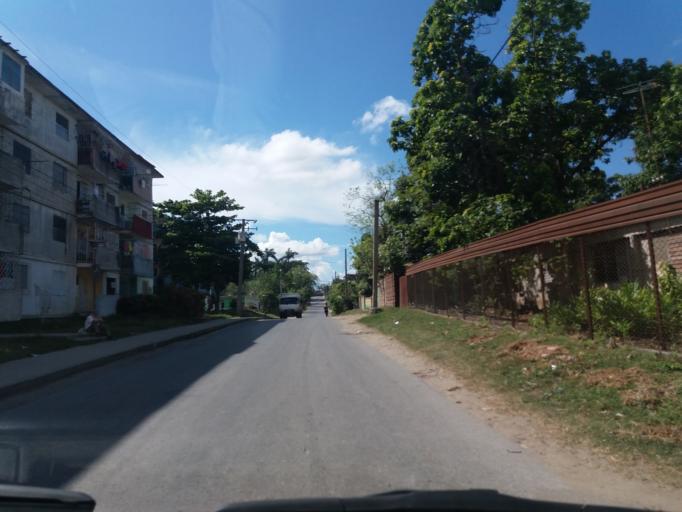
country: CU
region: Cienfuegos
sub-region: Municipio de Cienfuegos
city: Cienfuegos
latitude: 22.1500
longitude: -80.4273
